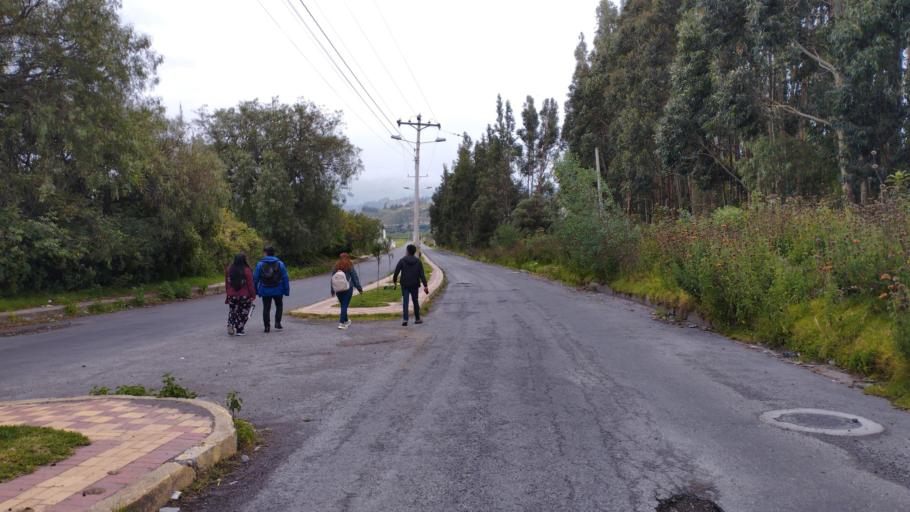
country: EC
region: Chimborazo
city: Guano
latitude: -1.6105
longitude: -78.6091
